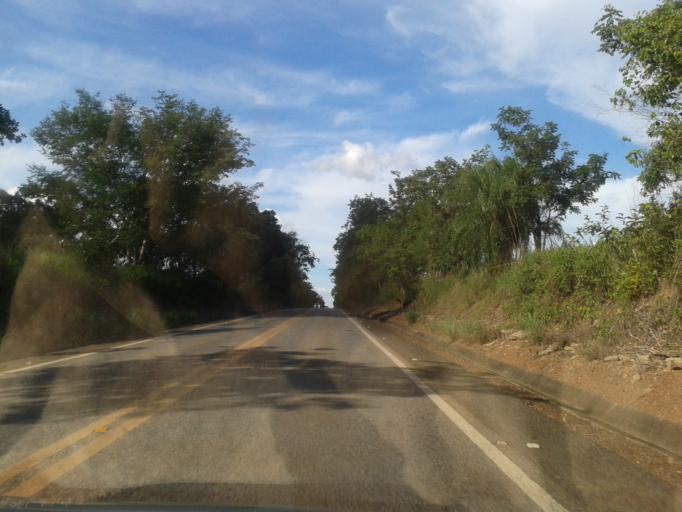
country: BR
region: Goias
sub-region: Mozarlandia
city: Mozarlandia
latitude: -14.5701
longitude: -50.5005
